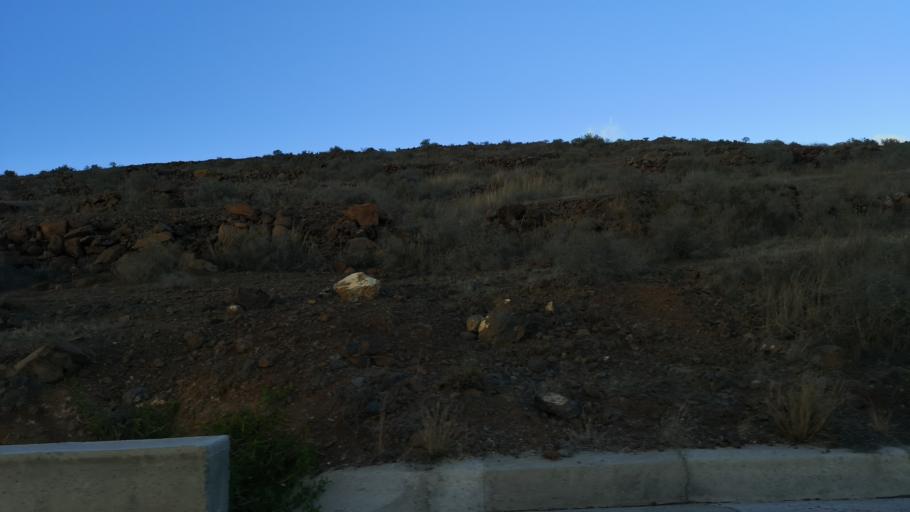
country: ES
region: Canary Islands
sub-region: Provincia de Santa Cruz de Tenerife
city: Alajero
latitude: 28.0396
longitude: -17.2290
